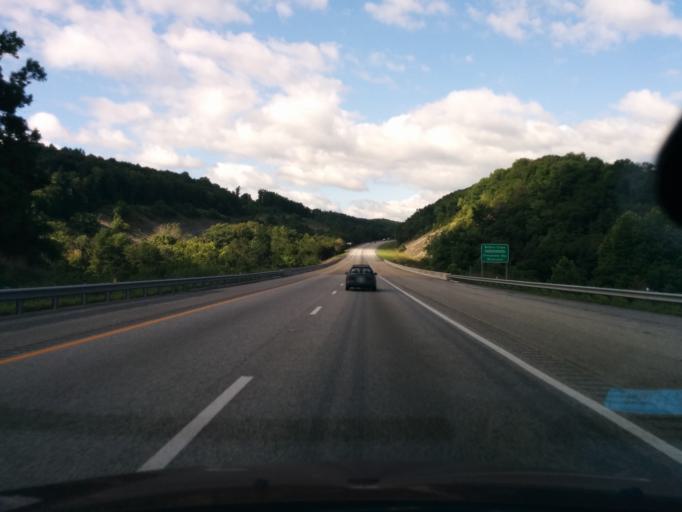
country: US
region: Virginia
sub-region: Rockbridge County
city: Glasgow
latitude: 37.7067
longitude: -79.4605
